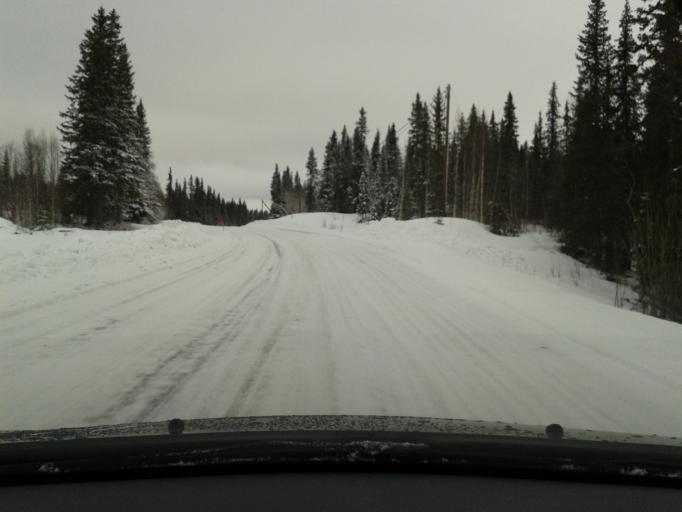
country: SE
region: Vaesterbotten
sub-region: Vilhelmina Kommun
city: Sjoberg
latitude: 65.2267
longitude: 15.9582
